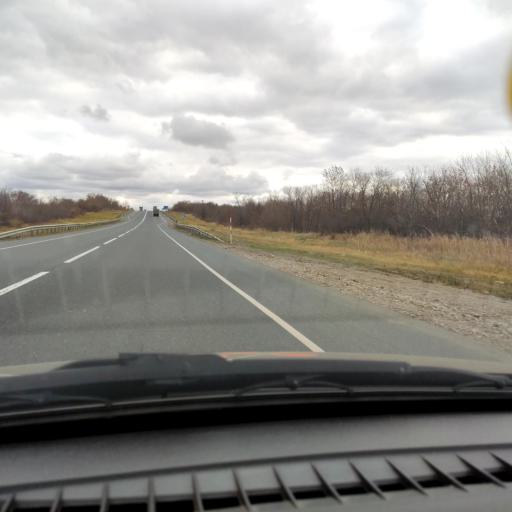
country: RU
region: Samara
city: Mezhdurechensk
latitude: 53.2570
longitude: 49.1187
